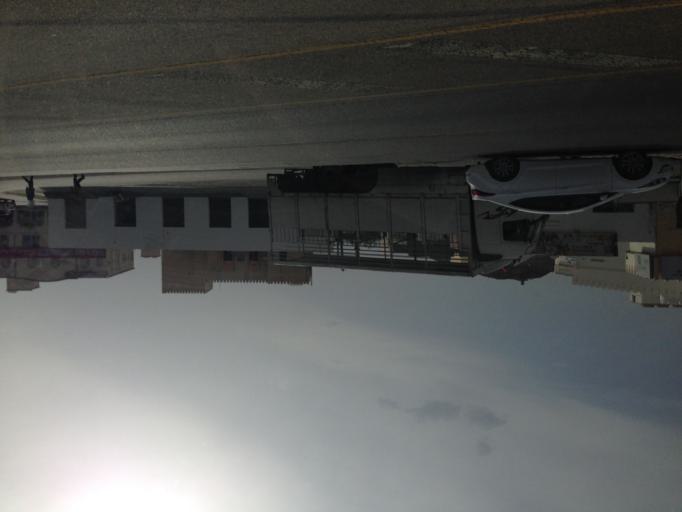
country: OM
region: Ash Sharqiyah
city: Al Qabil
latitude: 22.5839
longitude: 58.6868
